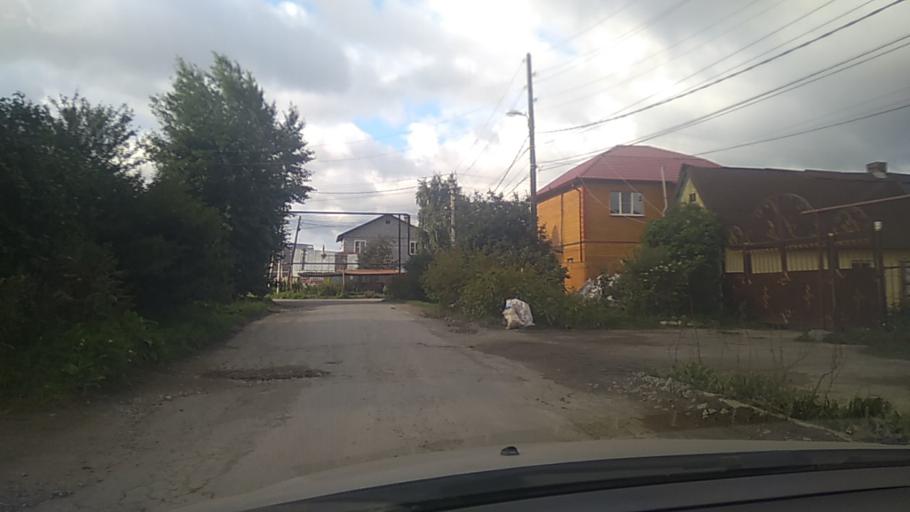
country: RU
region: Sverdlovsk
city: Shirokaya Rechka
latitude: 56.8032
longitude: 60.5026
